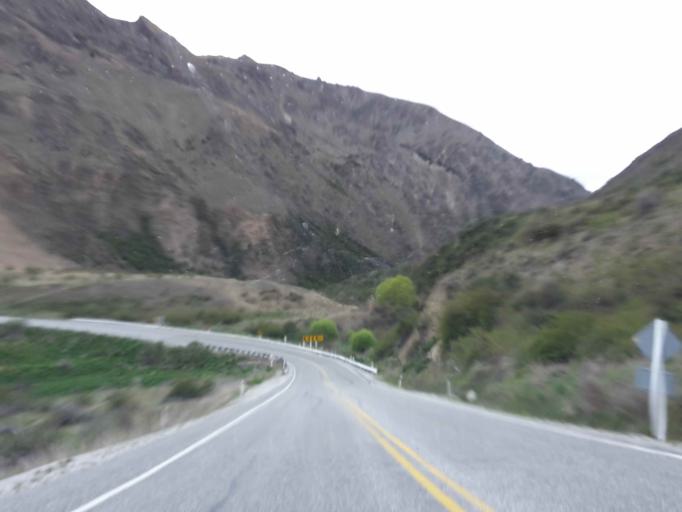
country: NZ
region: Otago
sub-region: Queenstown-Lakes District
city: Wanaka
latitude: -44.6095
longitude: 169.5415
